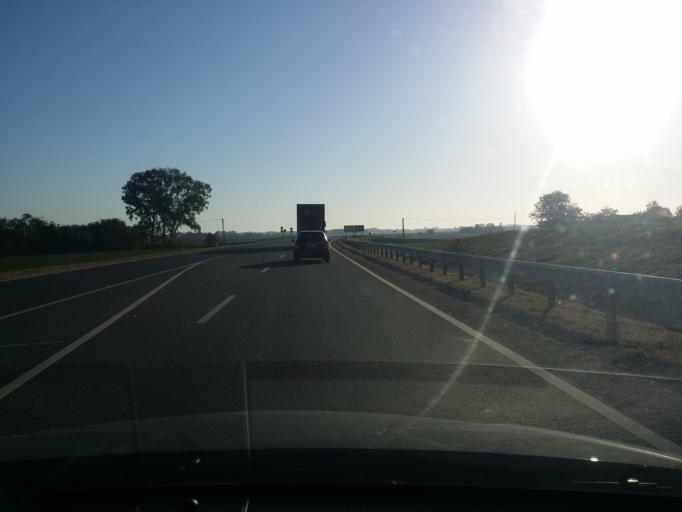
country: HU
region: Bacs-Kiskun
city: Kecskemet
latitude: 46.9505
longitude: 19.6793
